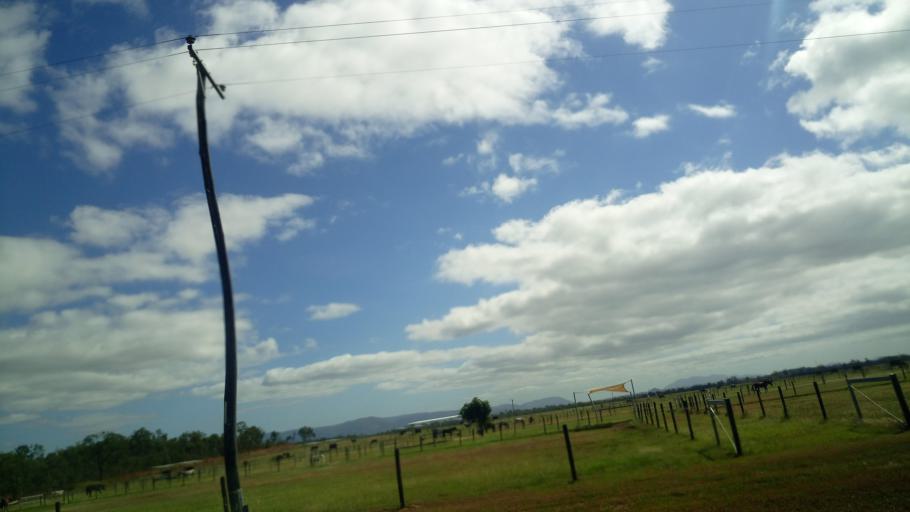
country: AU
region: Queensland
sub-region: Tablelands
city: Mareeba
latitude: -16.9736
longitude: 145.4579
